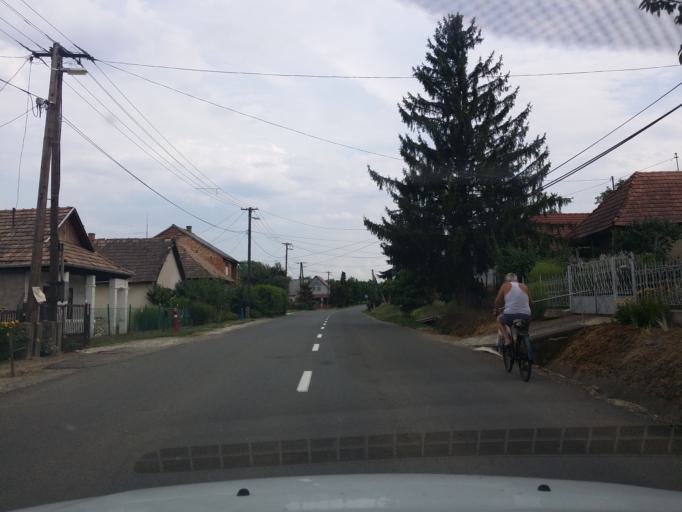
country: HU
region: Nograd
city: Romhany
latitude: 47.9642
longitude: 19.3514
